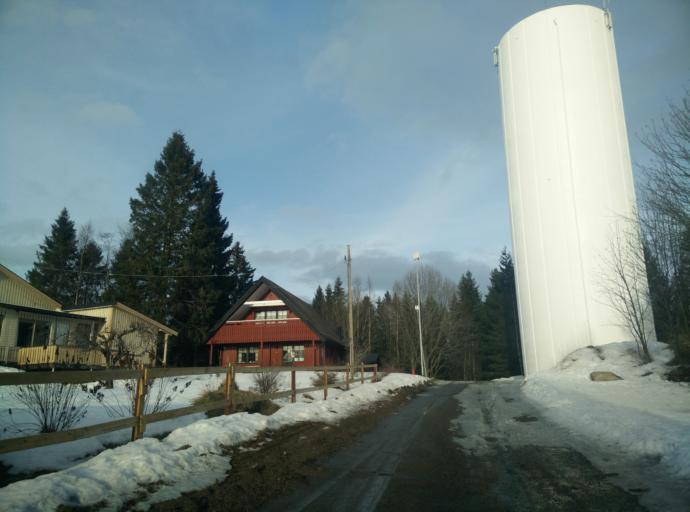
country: SE
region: Vaesternorrland
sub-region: Sundsvalls Kommun
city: Johannedal
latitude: 62.4346
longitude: 17.4197
